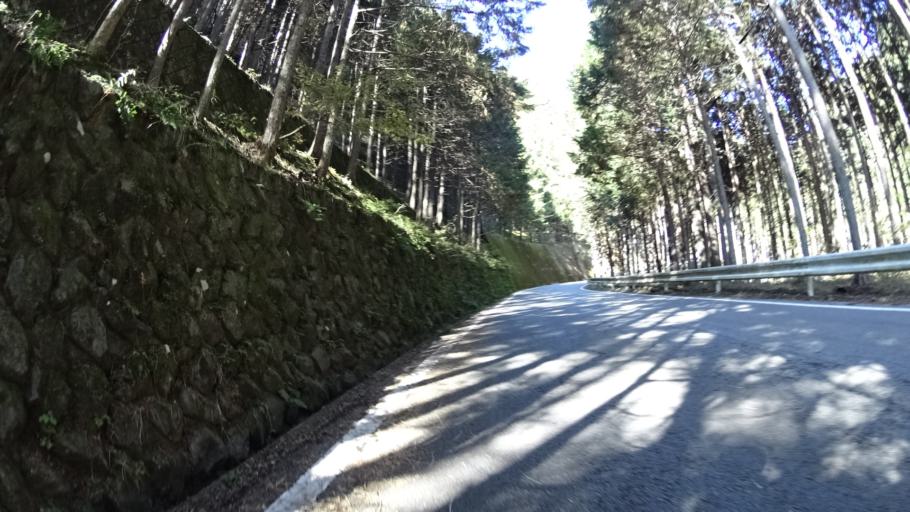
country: JP
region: Yamanashi
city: Otsuki
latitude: 35.7663
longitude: 138.9348
